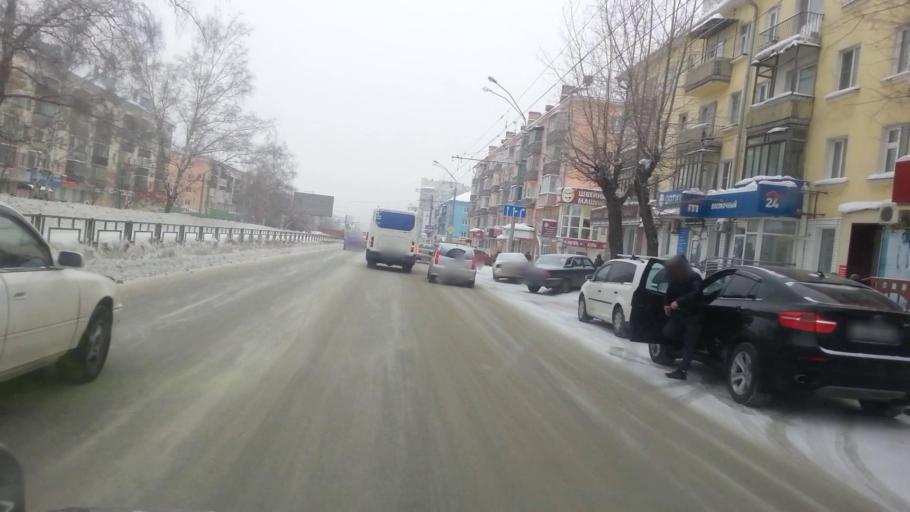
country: RU
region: Altai Krai
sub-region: Gorod Barnaulskiy
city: Barnaul
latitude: 53.3742
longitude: 83.7480
